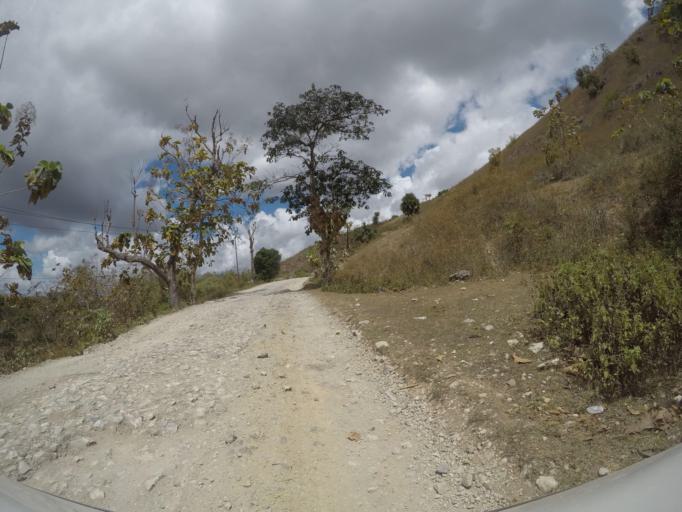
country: TL
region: Baucau
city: Baucau
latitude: -8.5161
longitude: 126.6886
